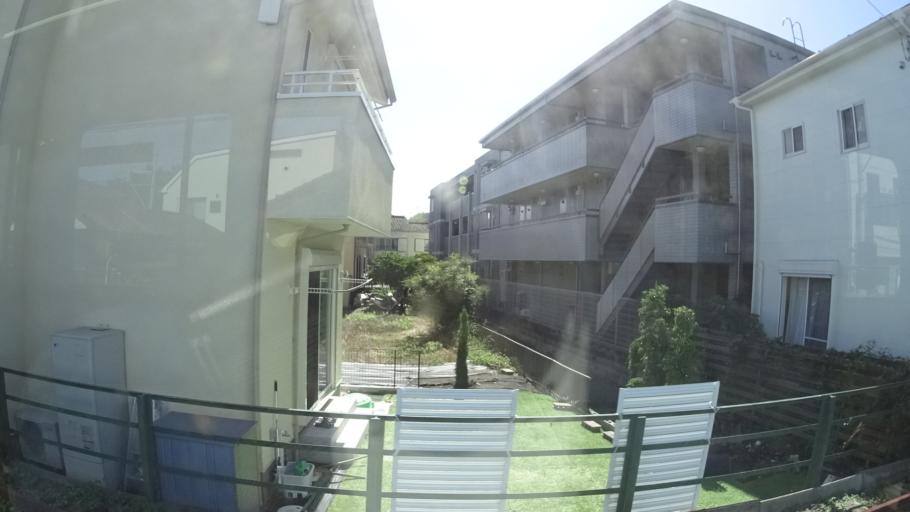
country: JP
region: Kanagawa
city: Fujisawa
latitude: 35.3304
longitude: 139.4853
